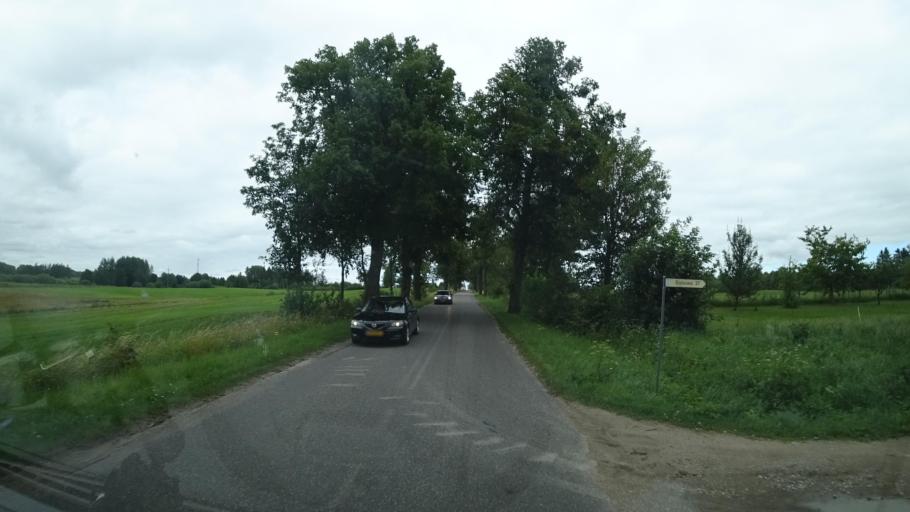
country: PL
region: Podlasie
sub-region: Powiat suwalski
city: Filipow
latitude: 54.2830
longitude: 22.5420
